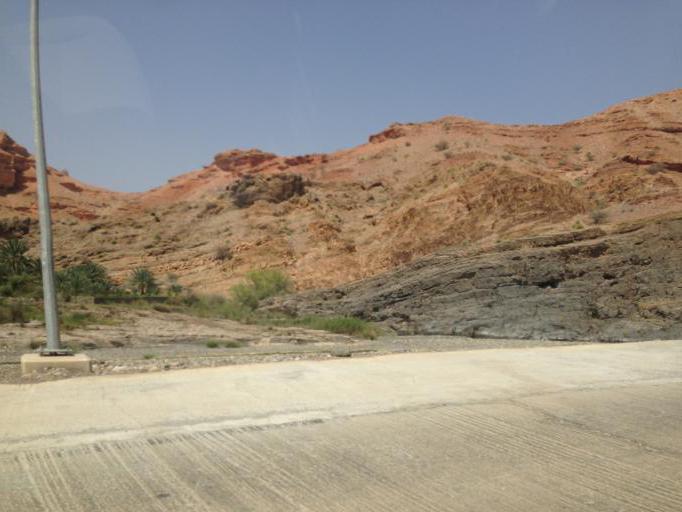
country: OM
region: Ash Sharqiyah
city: Ibra'
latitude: 23.0891
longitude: 58.8657
